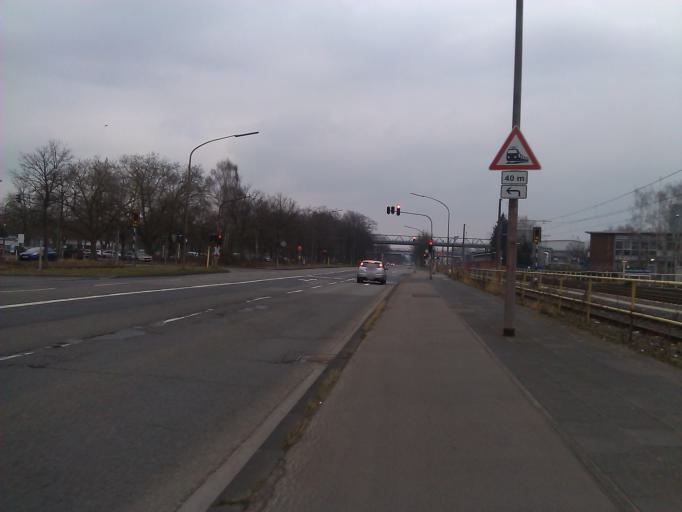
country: DE
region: North Rhine-Westphalia
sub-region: Regierungsbezirk Koln
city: Leverkusen
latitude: 51.0066
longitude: 6.9552
